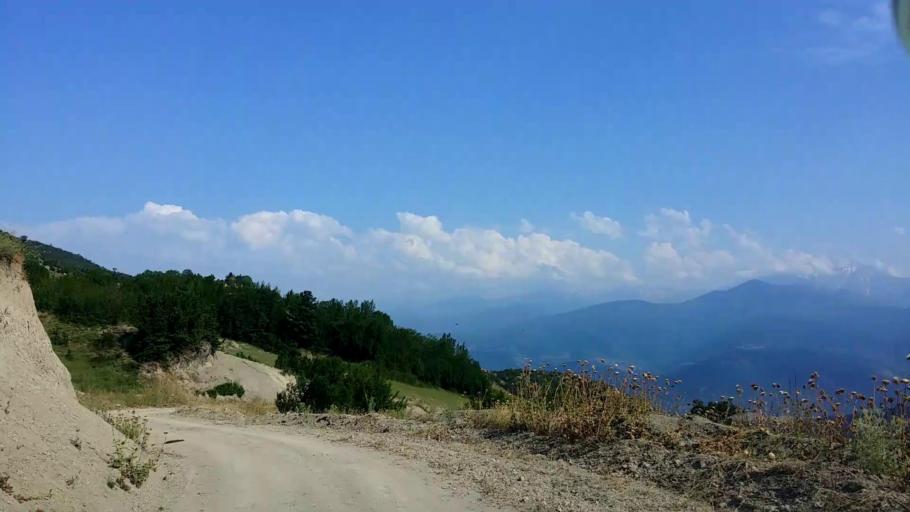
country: IR
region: Mazandaran
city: Chalus
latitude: 36.5482
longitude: 51.2961
